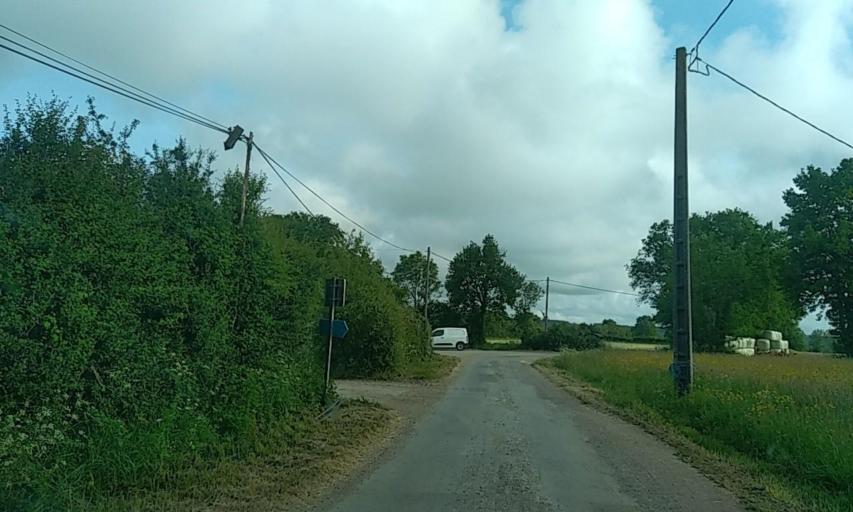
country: FR
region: Poitou-Charentes
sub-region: Departement des Deux-Sevres
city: Boisme
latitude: 46.7630
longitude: -0.4337
